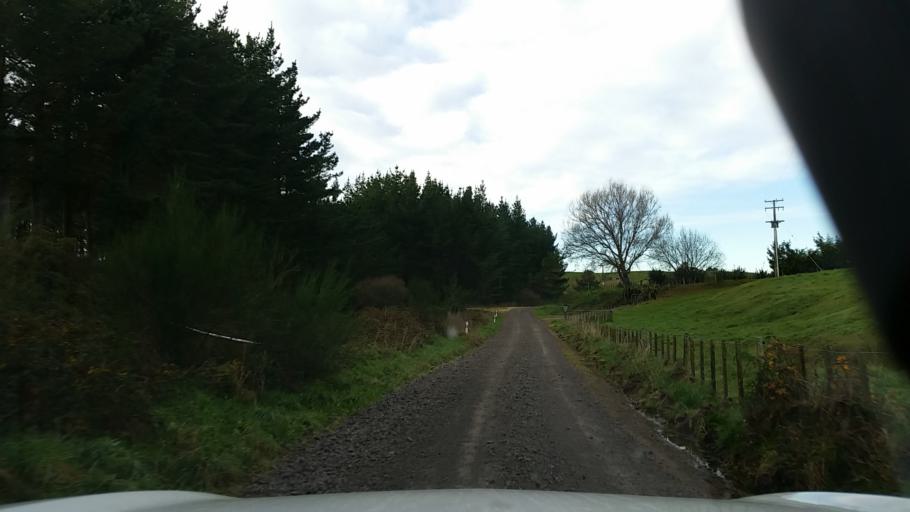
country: NZ
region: Bay of Plenty
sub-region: Rotorua District
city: Rotorua
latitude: -38.2691
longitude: 176.1553
